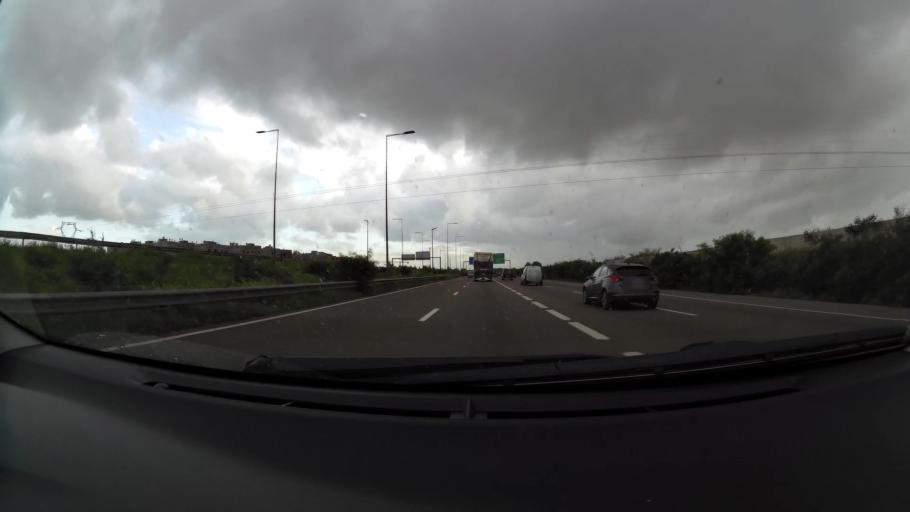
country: MA
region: Grand Casablanca
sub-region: Mohammedia
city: Mohammedia
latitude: 33.6539
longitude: -7.4136
